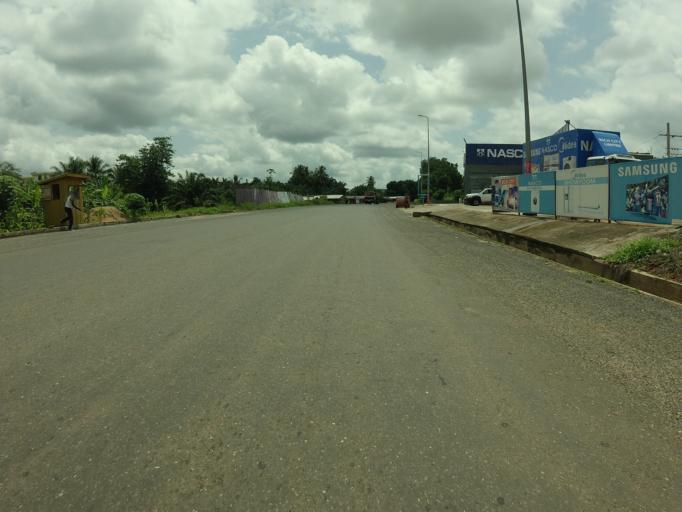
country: GH
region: Volta
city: Ho
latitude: 6.5910
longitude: 0.4725
